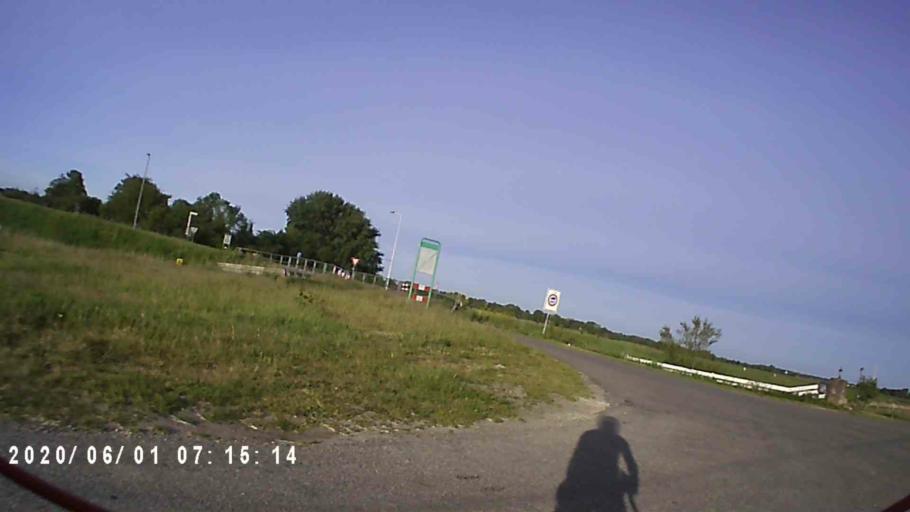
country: NL
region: Friesland
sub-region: Gemeente Dantumadiel
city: Walterswald
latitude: 53.3143
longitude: 6.0469
